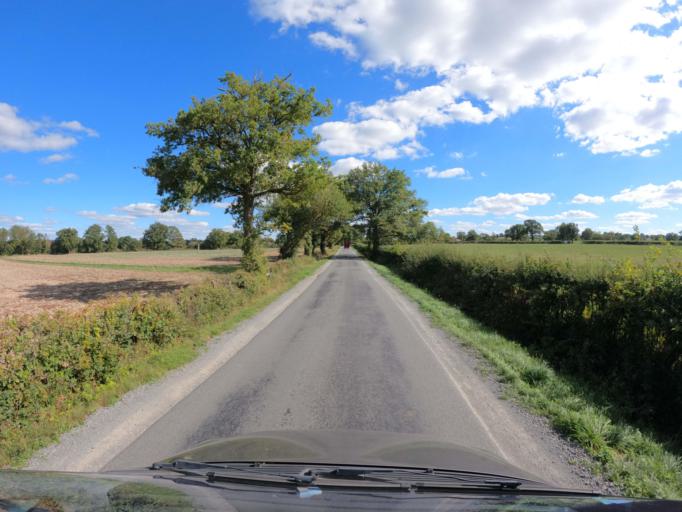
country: FR
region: Auvergne
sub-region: Departement de l'Allier
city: Doyet
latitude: 46.3924
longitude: 2.7564
